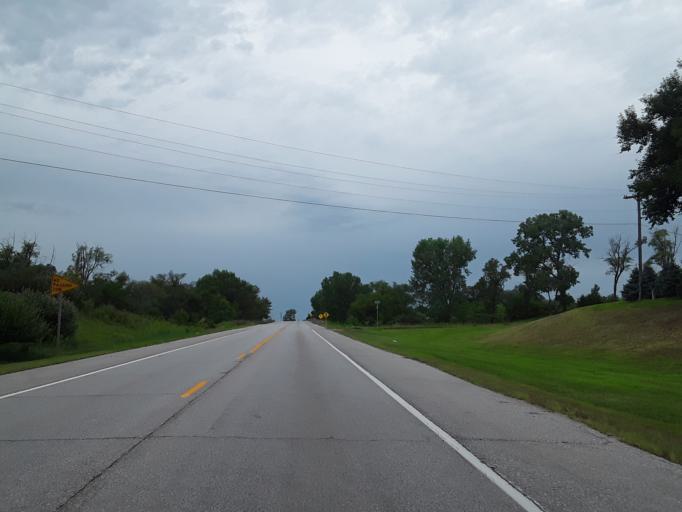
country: US
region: Iowa
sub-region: Pottawattamie County
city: Carter Lake
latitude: 41.3618
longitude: -96.0186
